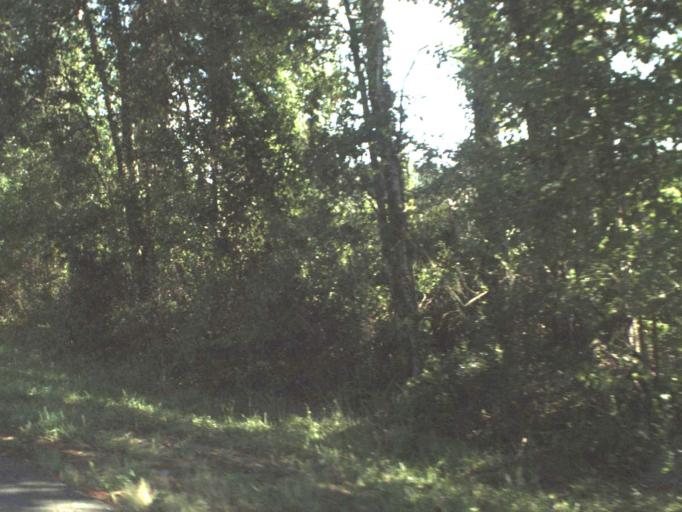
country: US
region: Florida
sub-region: Lake County
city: Four Corners
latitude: 28.3680
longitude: -81.8209
